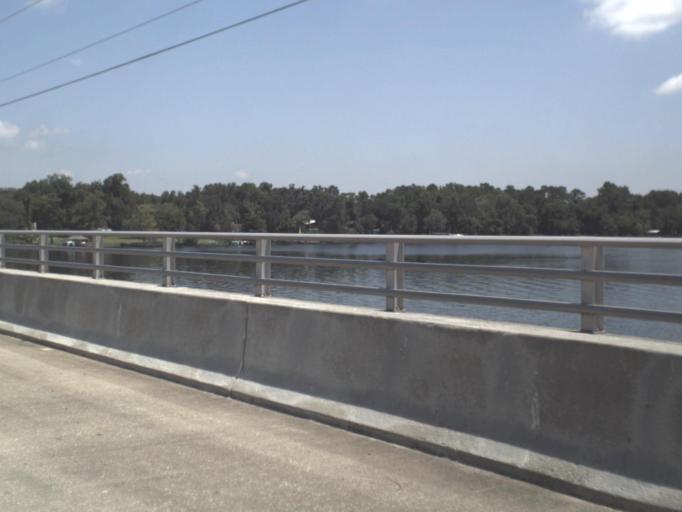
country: US
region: Florida
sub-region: Saint Johns County
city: Fruit Cove
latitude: 30.1312
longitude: -81.6287
